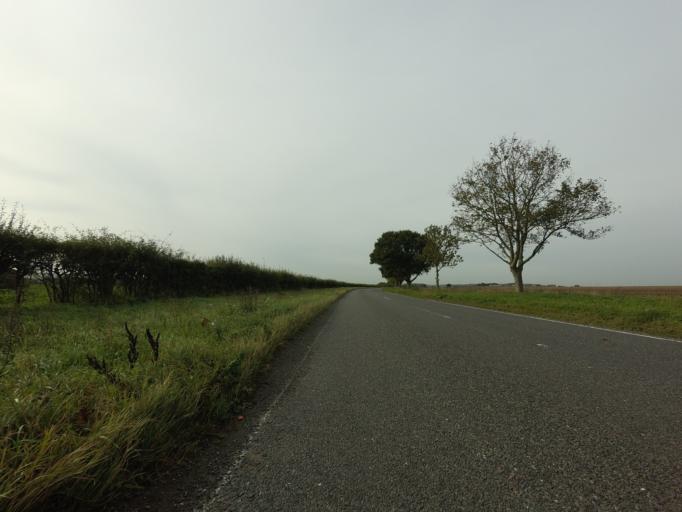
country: GB
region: England
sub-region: Cambridgeshire
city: Melbourn
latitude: 52.0755
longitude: 0.0649
